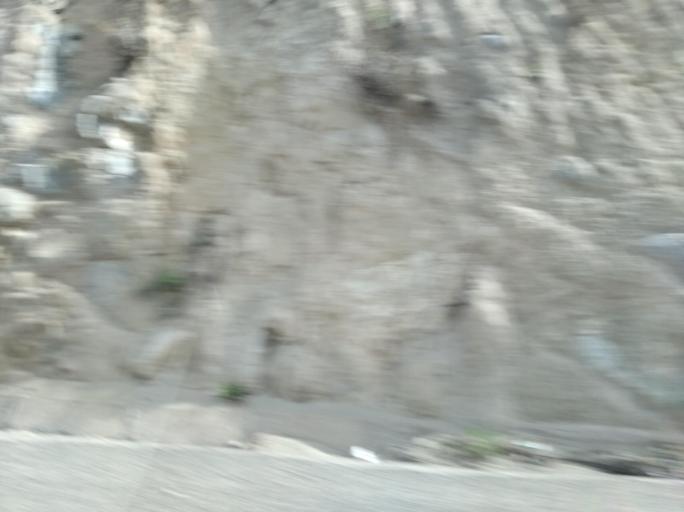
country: CL
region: Valparaiso
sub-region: Provincia de San Felipe
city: Llaillay
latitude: -33.0641
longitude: -71.0128
